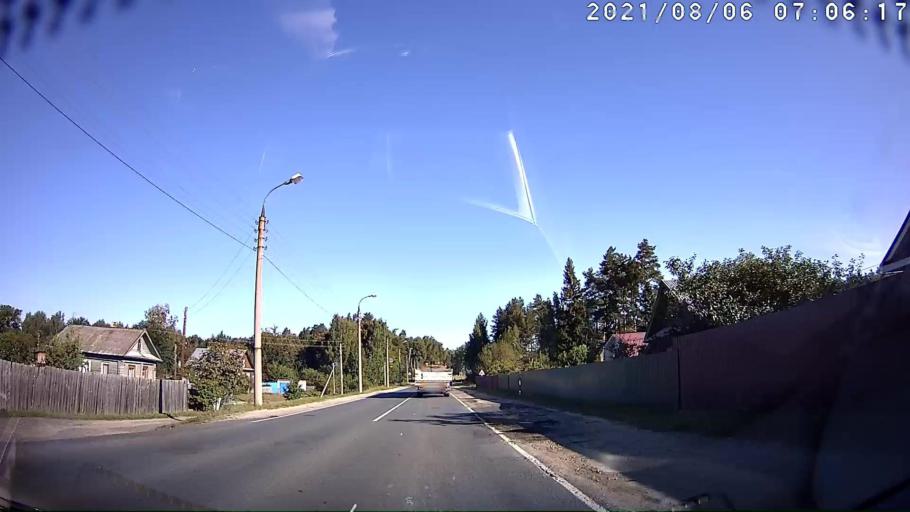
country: RU
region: Mariy-El
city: Yoshkar-Ola
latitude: 56.5579
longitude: 47.9820
